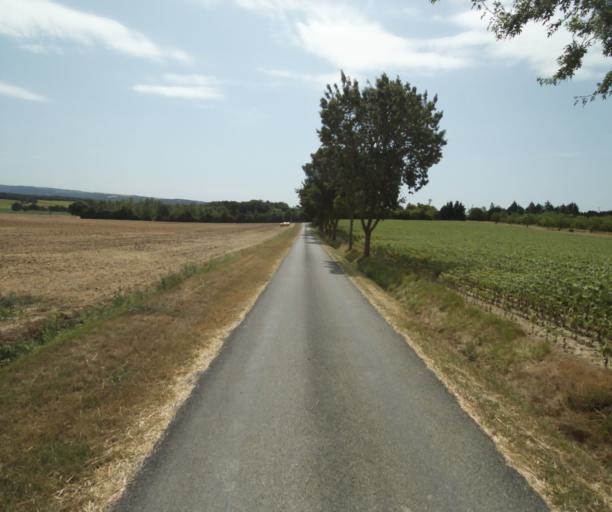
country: FR
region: Midi-Pyrenees
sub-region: Departement de la Haute-Garonne
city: Saint-Felix-Lauragais
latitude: 43.4256
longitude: 1.9127
